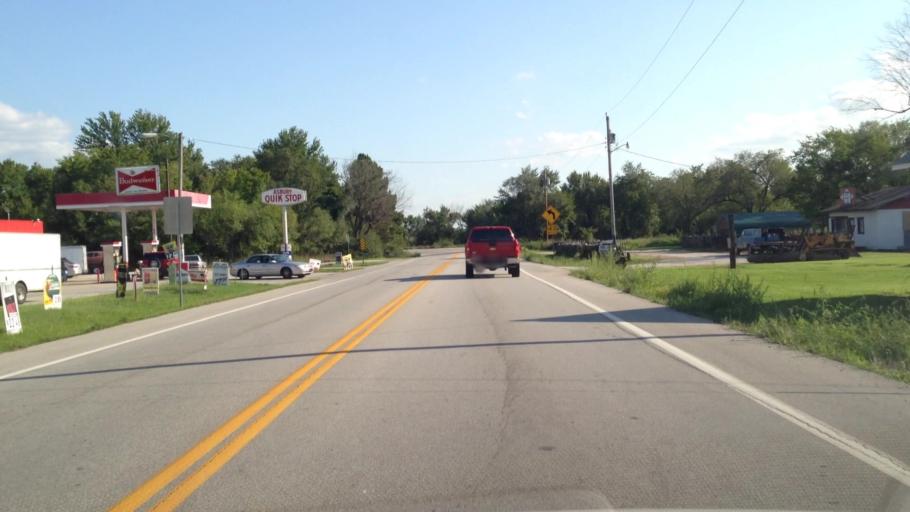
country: US
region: Missouri
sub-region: Jasper County
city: Carl Junction
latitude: 37.2743
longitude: -94.6011
